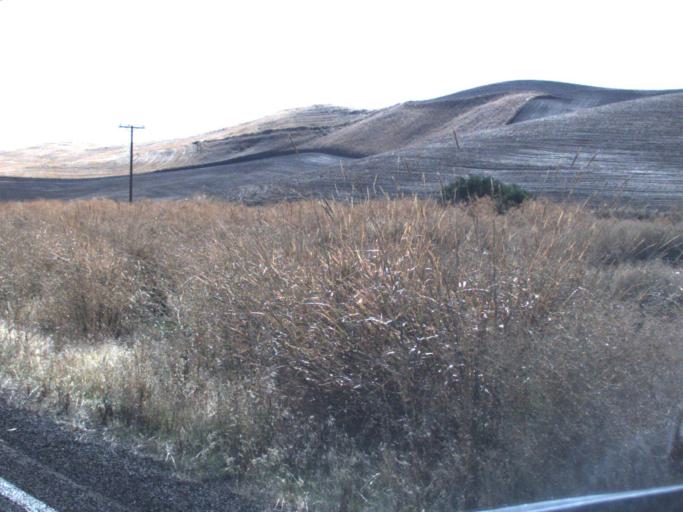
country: US
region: Washington
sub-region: Walla Walla County
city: Walla Walla
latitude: 46.2058
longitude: -118.3867
